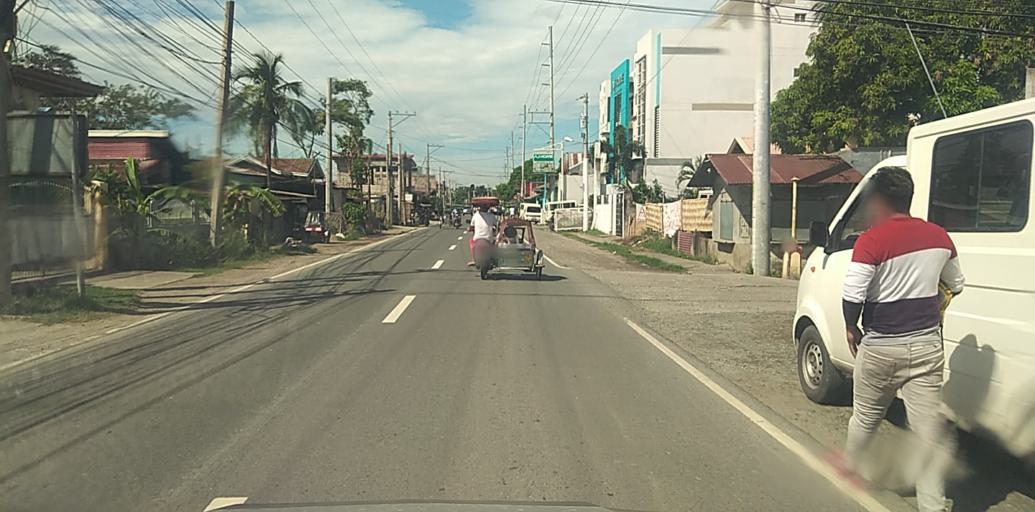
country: PH
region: Central Luzon
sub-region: Province of Pampanga
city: Arayat
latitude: 15.1474
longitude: 120.7623
